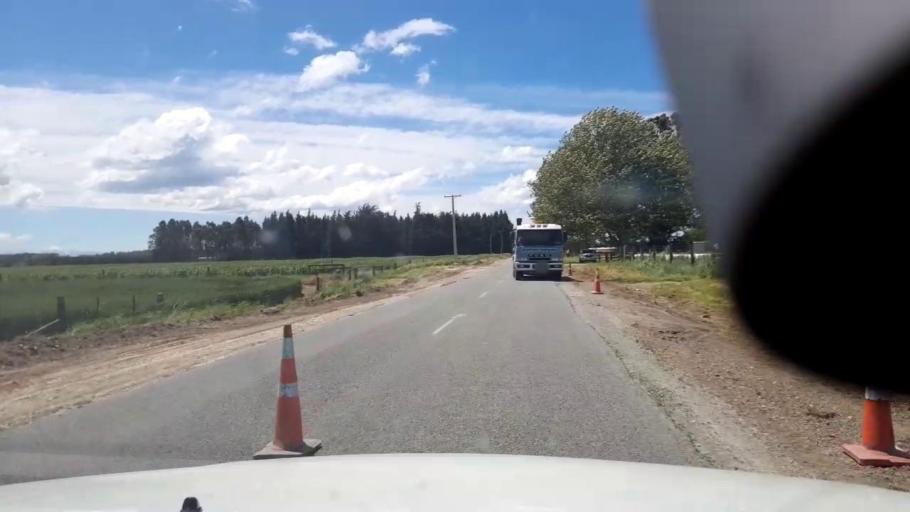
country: NZ
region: Canterbury
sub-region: Timaru District
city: Pleasant Point
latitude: -44.2783
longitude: 171.2485
